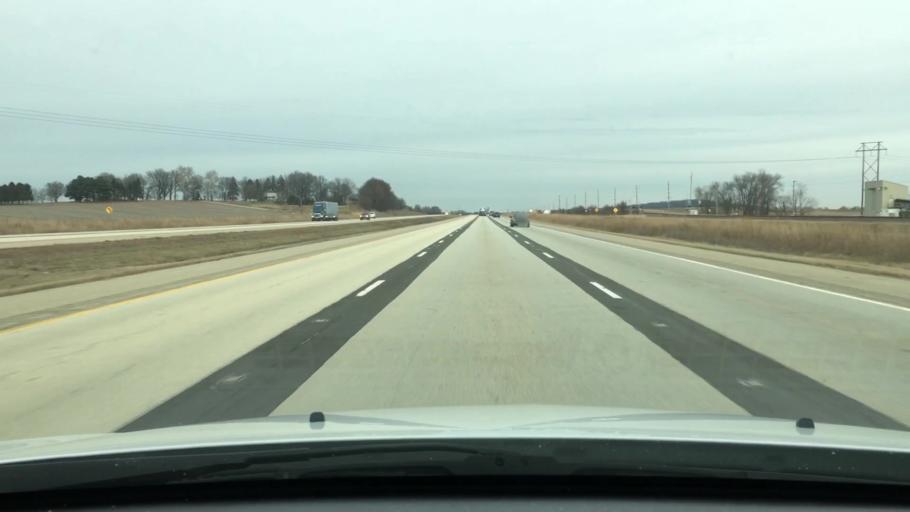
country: US
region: Illinois
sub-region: Sangamon County
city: Williamsville
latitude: 39.9901
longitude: -89.5149
